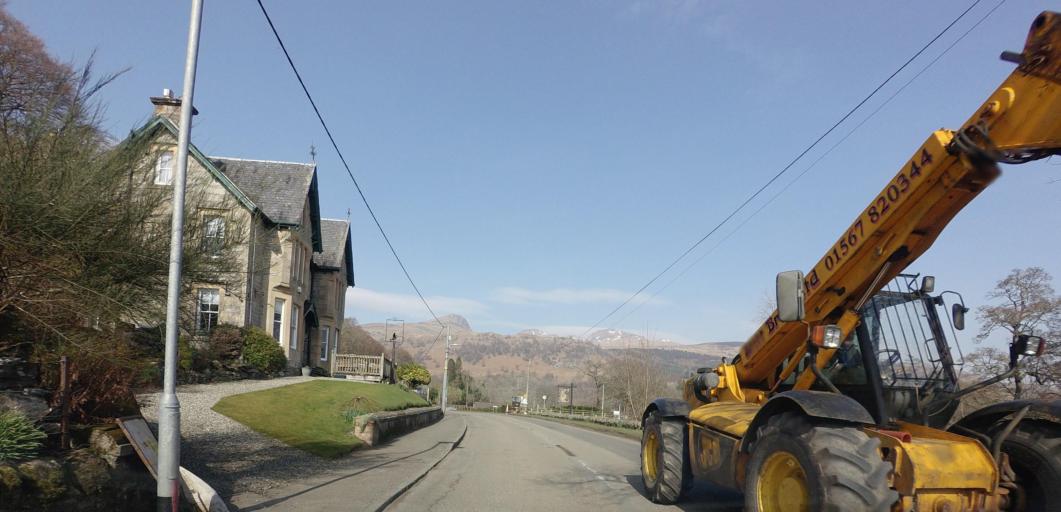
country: GB
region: Scotland
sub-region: Stirling
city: Callander
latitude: 56.4725
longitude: -4.3212
